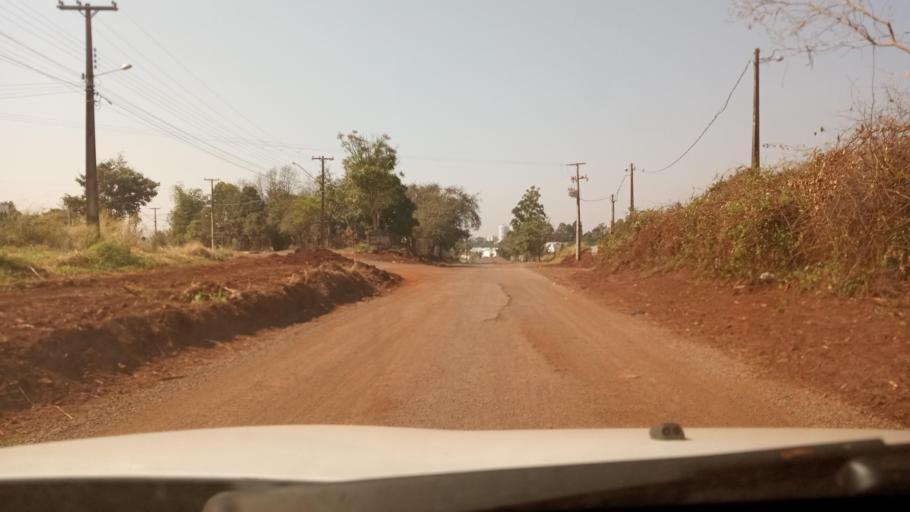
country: BR
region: Parana
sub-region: Toledo
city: Toledo
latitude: -24.7103
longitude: -53.7595
